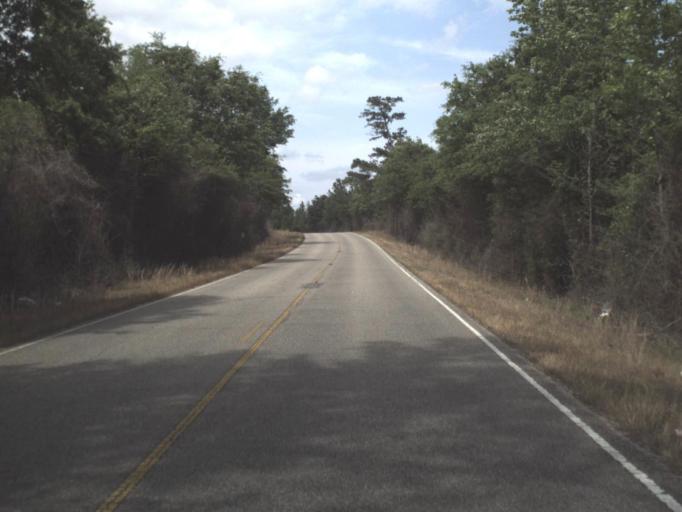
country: US
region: Alabama
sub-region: Escambia County
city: East Brewton
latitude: 31.0010
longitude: -87.1147
